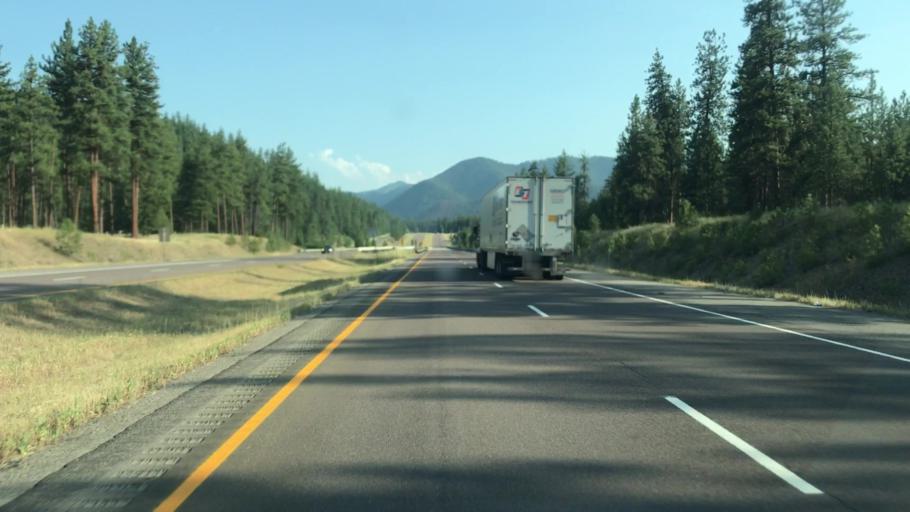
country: US
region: Montana
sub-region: Mineral County
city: Superior
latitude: 47.0716
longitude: -114.7654
